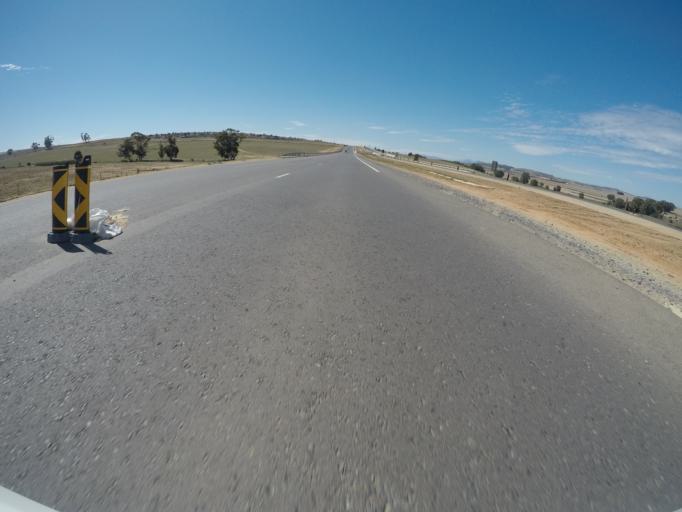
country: ZA
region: Western Cape
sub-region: West Coast District Municipality
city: Malmesbury
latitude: -33.4777
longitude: 18.6859
